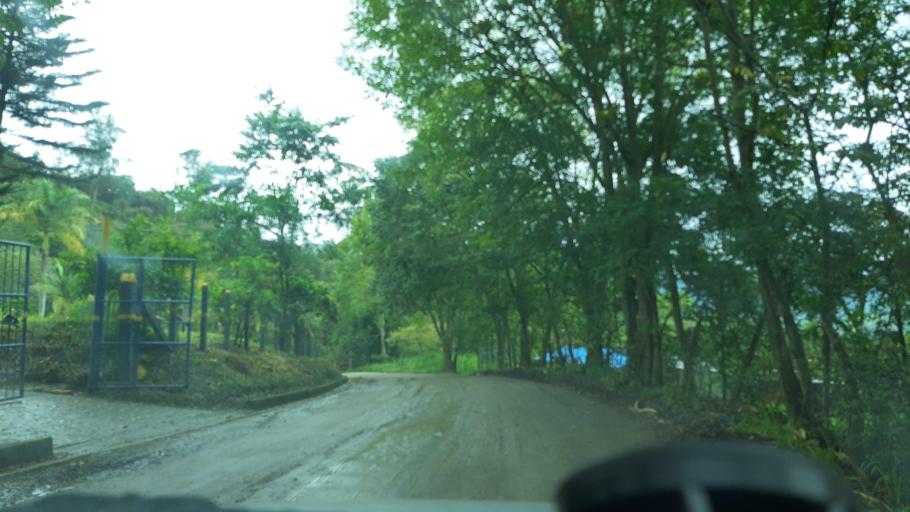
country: CO
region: Cundinamarca
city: Manta
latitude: 5.0488
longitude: -73.5102
